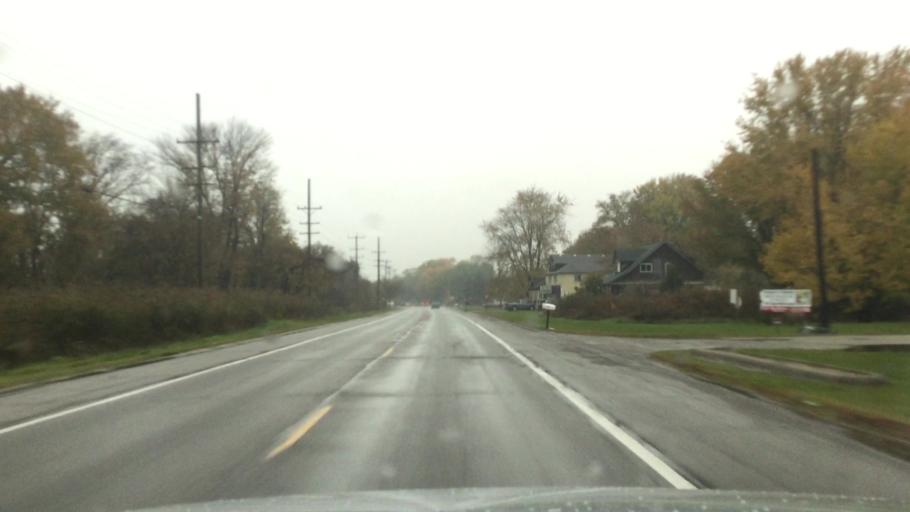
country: US
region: Michigan
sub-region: Saint Clair County
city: Pearl Beach
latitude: 42.6756
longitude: -82.6324
